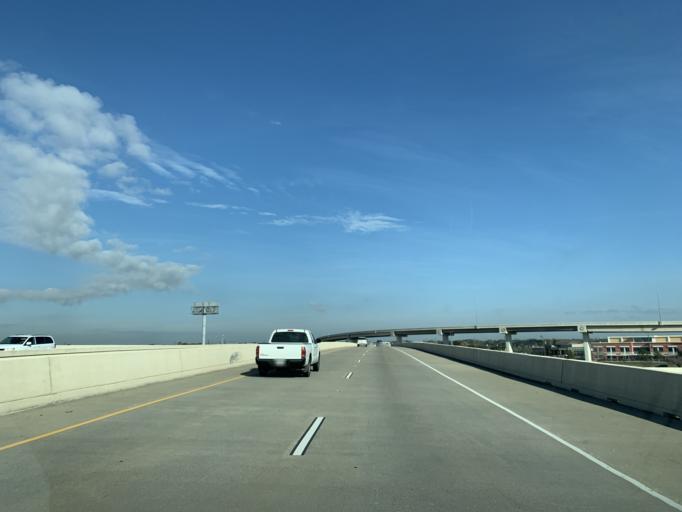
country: US
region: Texas
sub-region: Fort Bend County
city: Cinco Ranch
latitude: 29.6990
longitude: -95.7754
